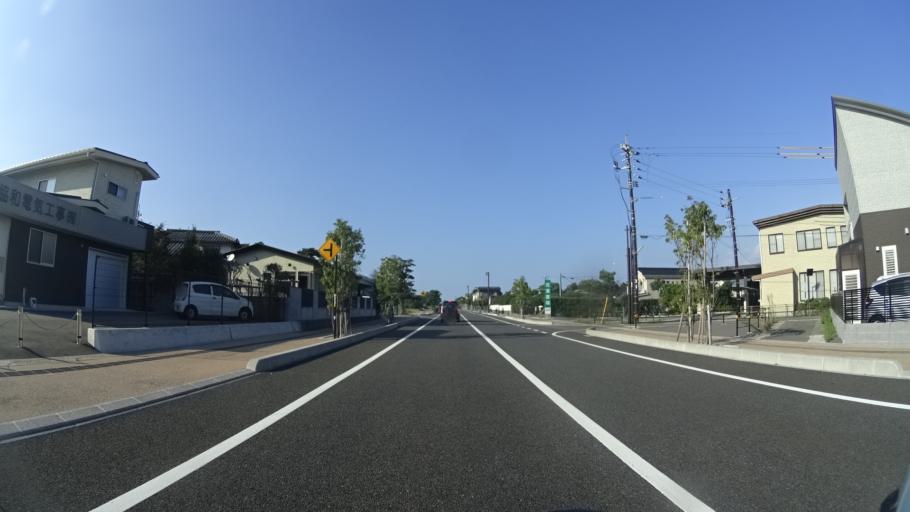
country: JP
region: Yamaguchi
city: Hagi
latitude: 34.4095
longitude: 131.3914
